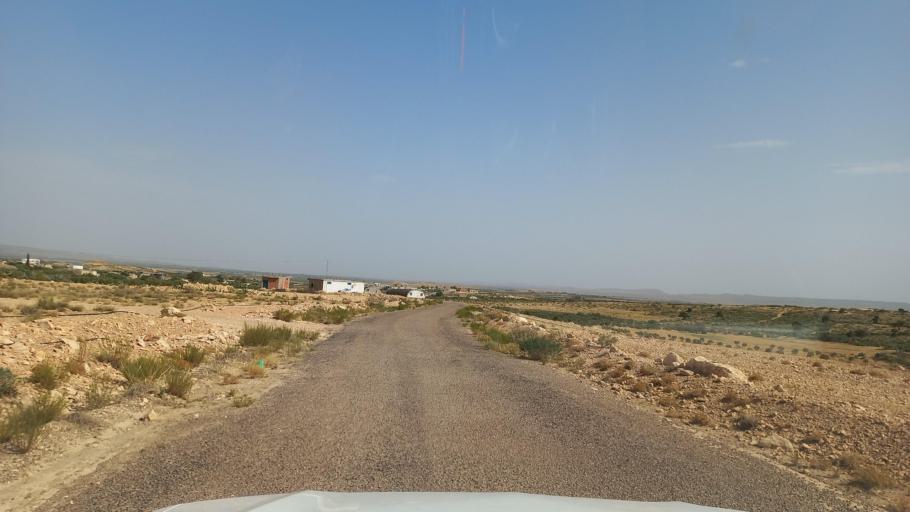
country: TN
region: Al Qasrayn
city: Kasserine
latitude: 35.3043
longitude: 8.9418
